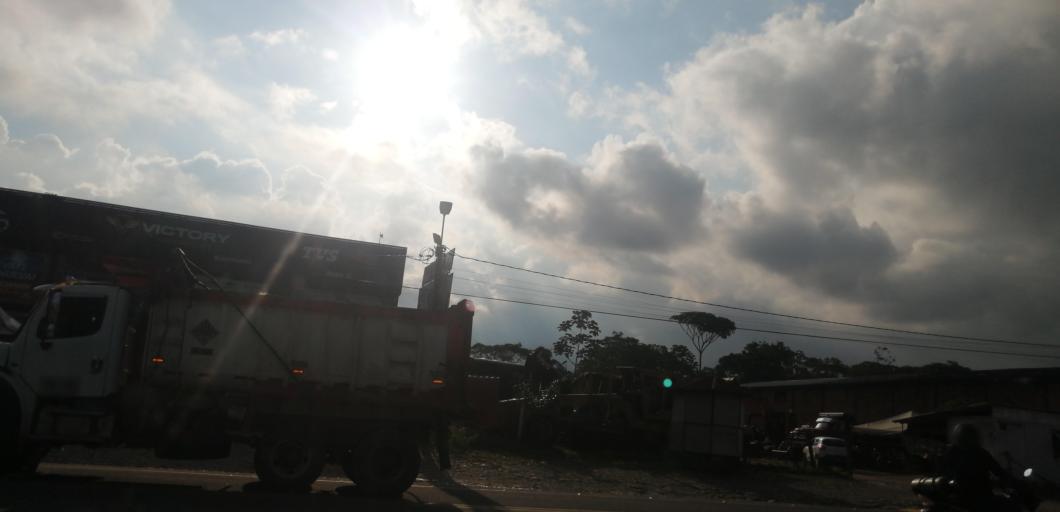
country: CO
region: Meta
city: Acacias
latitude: 3.9780
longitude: -73.7668
